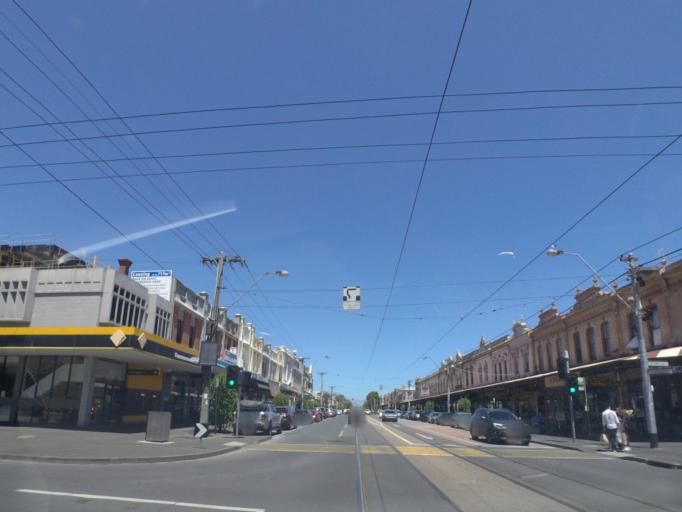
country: AU
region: Victoria
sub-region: Port Phillip
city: South Melbourne
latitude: -37.8328
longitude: 144.9605
